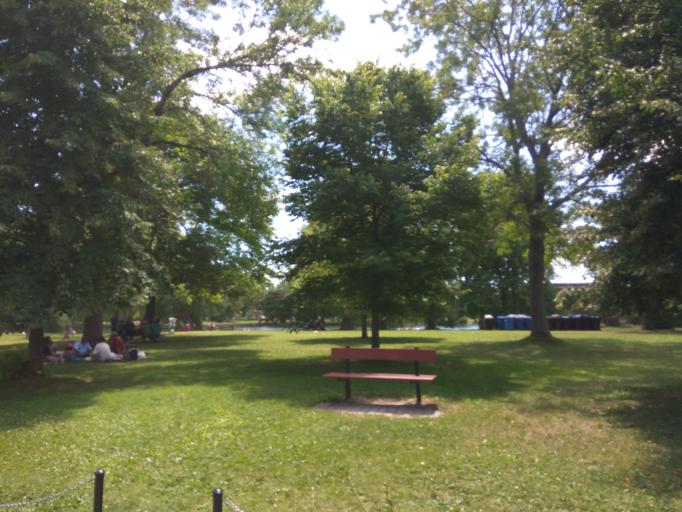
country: CA
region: Ontario
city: Toronto
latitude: 43.6201
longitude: -79.3755
